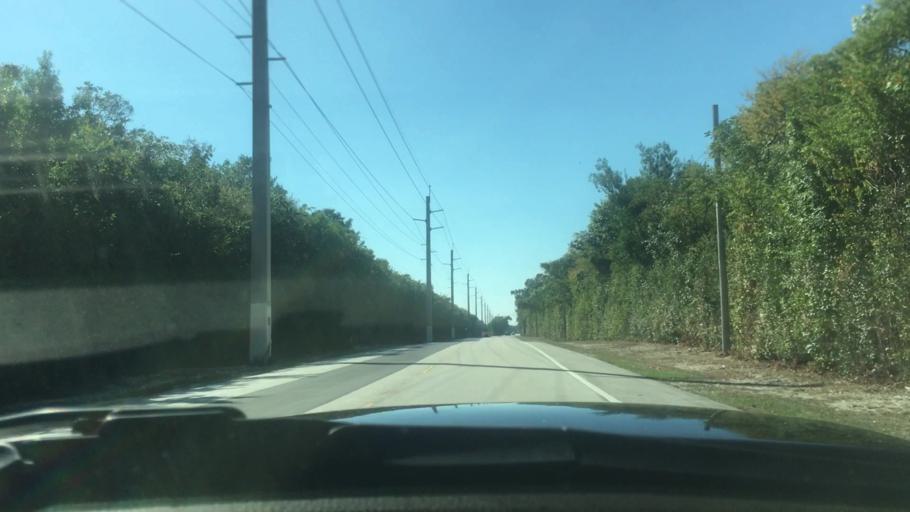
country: US
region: Florida
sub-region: Monroe County
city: North Key Largo
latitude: 25.2158
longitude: -80.3378
